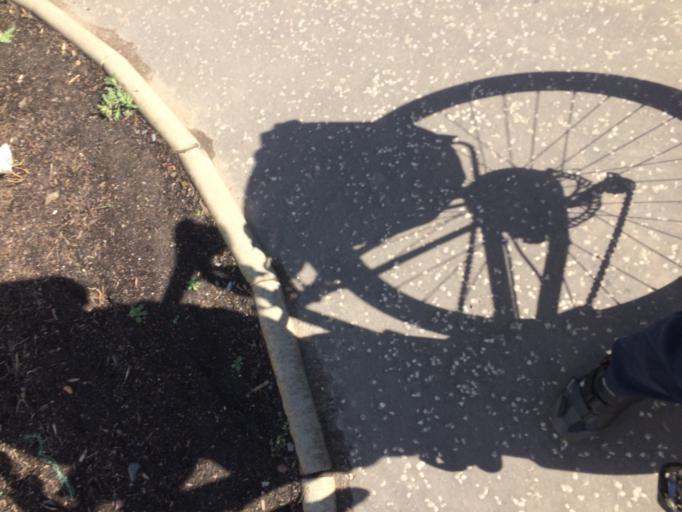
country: GB
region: Scotland
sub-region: East Lothian
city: Musselburgh
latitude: 55.9367
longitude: -3.0864
